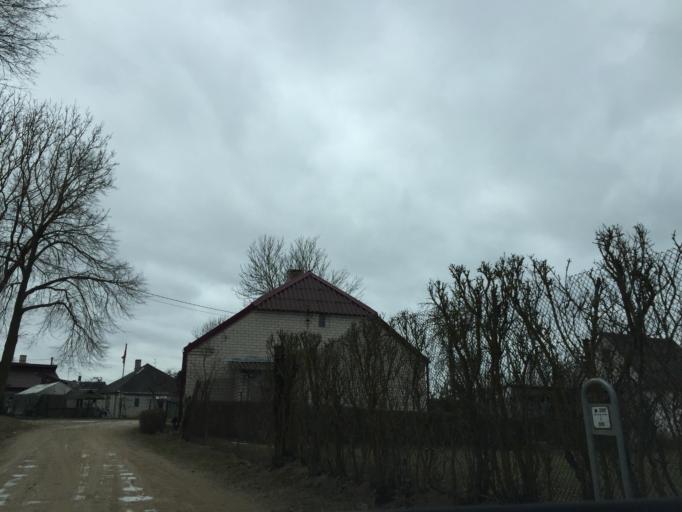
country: LT
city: Zagare
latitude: 56.3616
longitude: 23.2519
